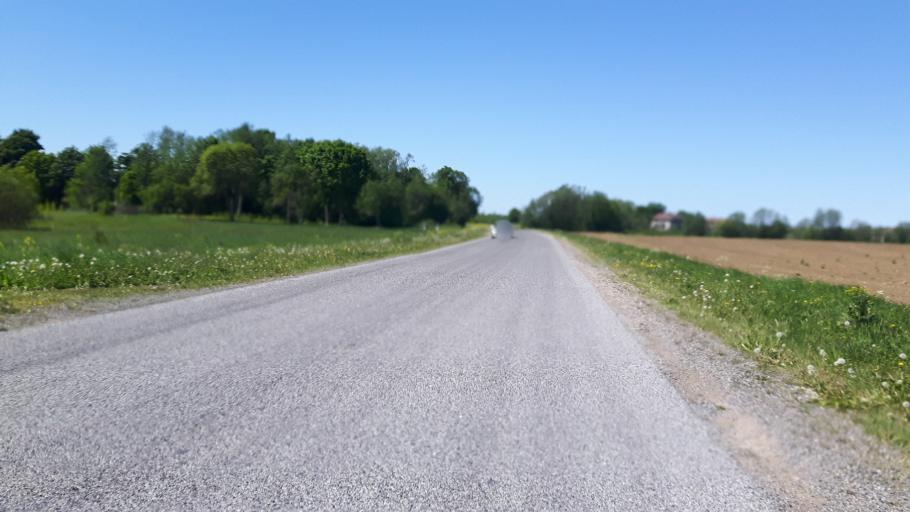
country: EE
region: Ida-Virumaa
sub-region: Sillamaee linn
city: Sillamae
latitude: 59.3822
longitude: 27.8221
